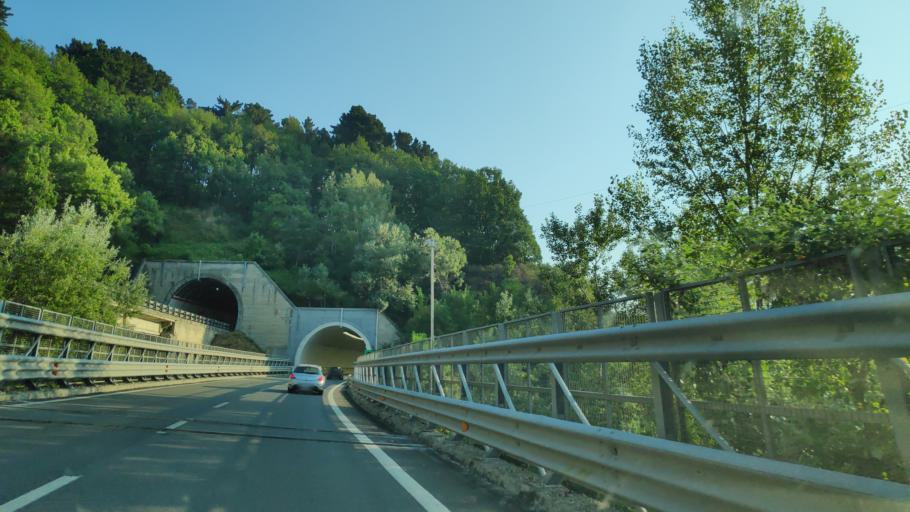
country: IT
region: Calabria
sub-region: Provincia di Cosenza
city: Belsito
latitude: 39.1745
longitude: 16.2939
